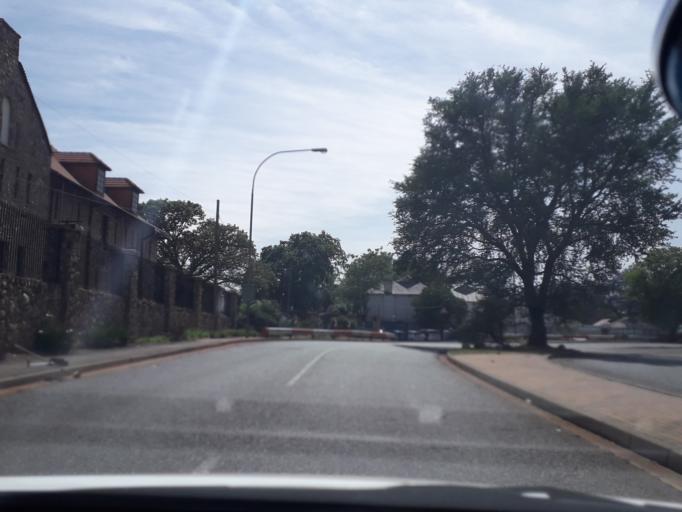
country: ZA
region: Gauteng
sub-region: City of Johannesburg Metropolitan Municipality
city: Johannesburg
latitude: -26.1779
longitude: 28.0565
